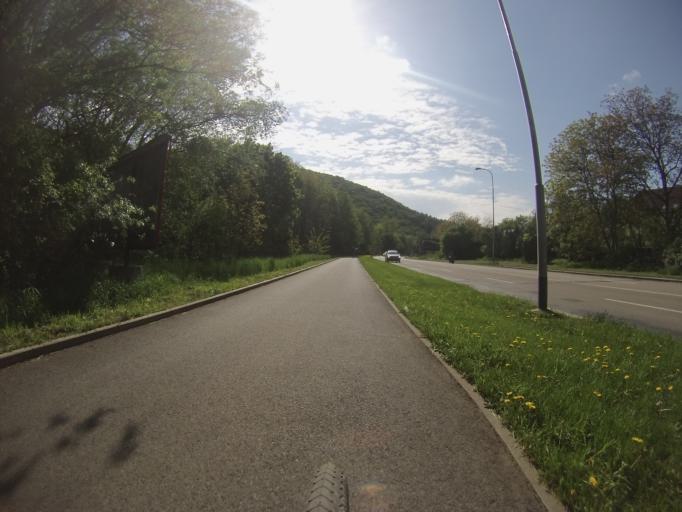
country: CZ
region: South Moravian
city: Ostopovice
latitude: 49.2185
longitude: 16.5454
